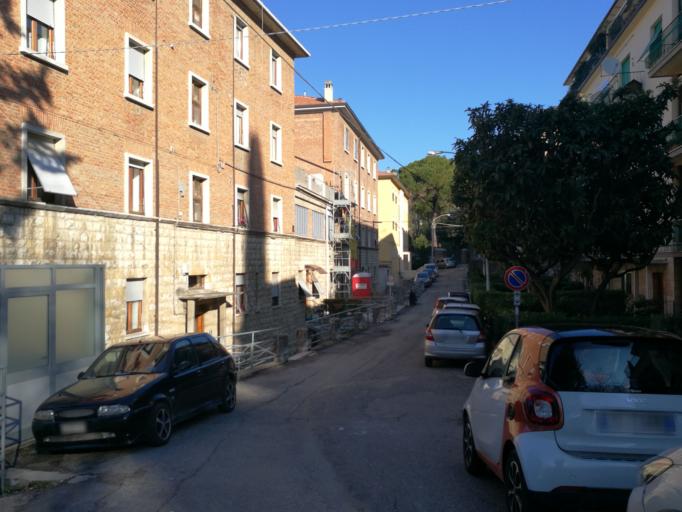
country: IT
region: Umbria
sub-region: Provincia di Perugia
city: Perugia
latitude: 43.0997
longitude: 12.3934
